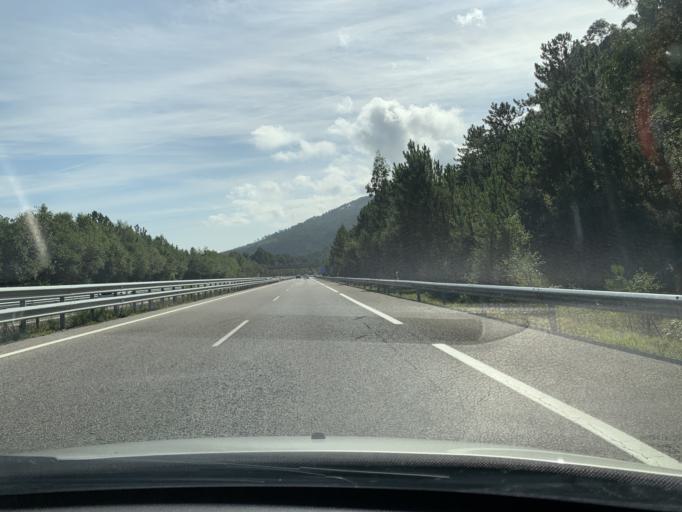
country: ES
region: Asturias
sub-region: Province of Asturias
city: Salas
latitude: 43.5447
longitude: -6.3481
